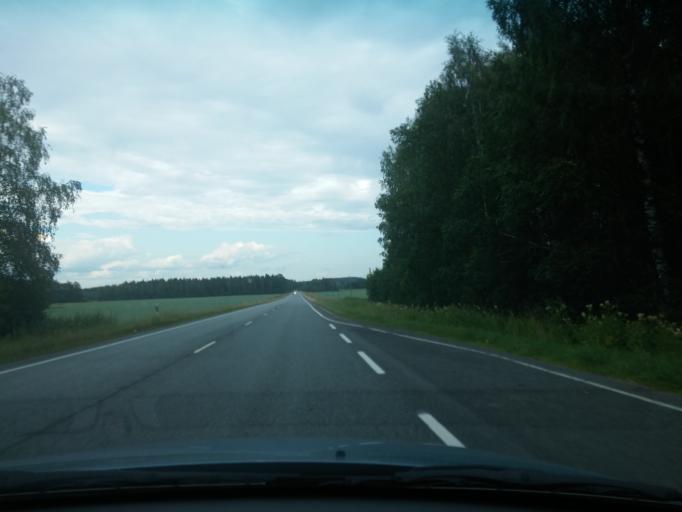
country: FI
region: Haeme
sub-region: Haemeenlinna
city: Tervakoski
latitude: 60.7397
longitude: 24.6061
